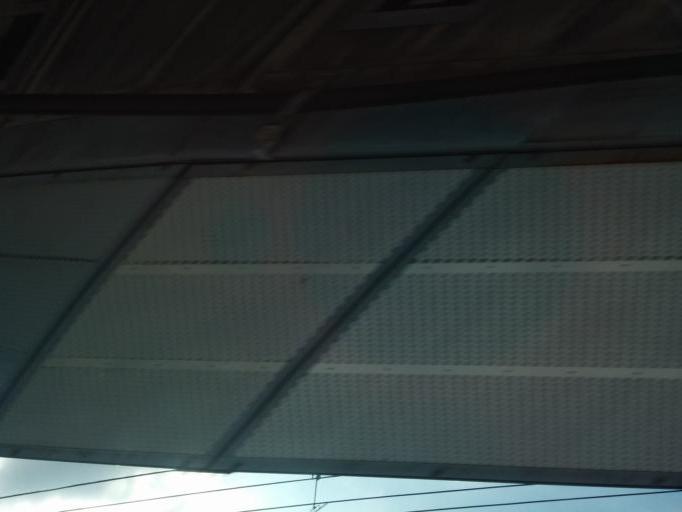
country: JP
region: Kanagawa
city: Yugawara
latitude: 35.1561
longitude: 139.1076
